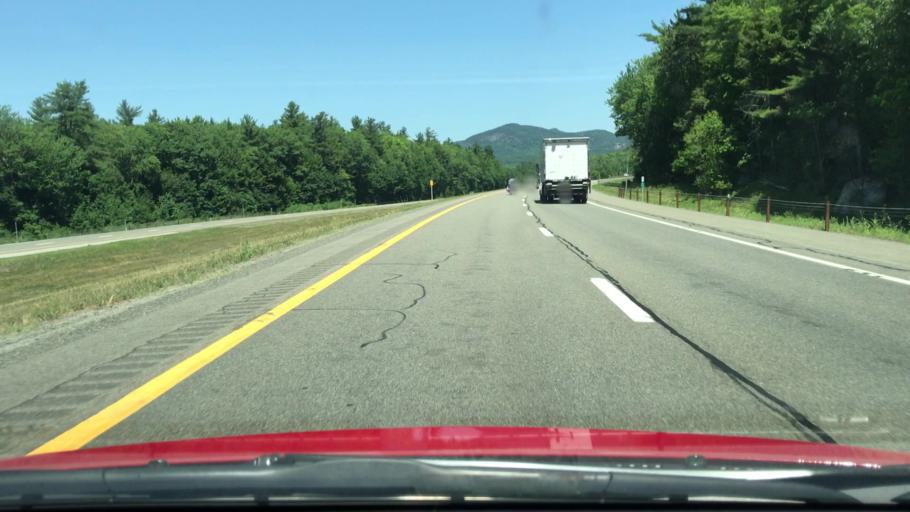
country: US
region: New York
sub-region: Essex County
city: Elizabethtown
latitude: 44.3353
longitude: -73.5333
